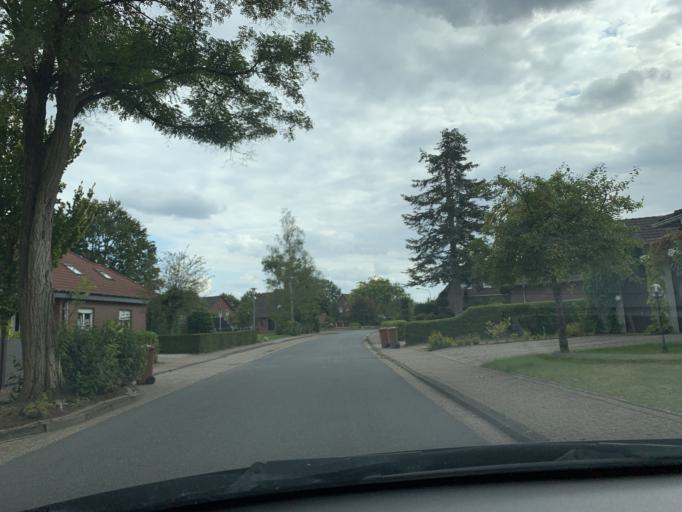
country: DE
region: Lower Saxony
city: Westerstede
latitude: 53.2558
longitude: 7.9420
